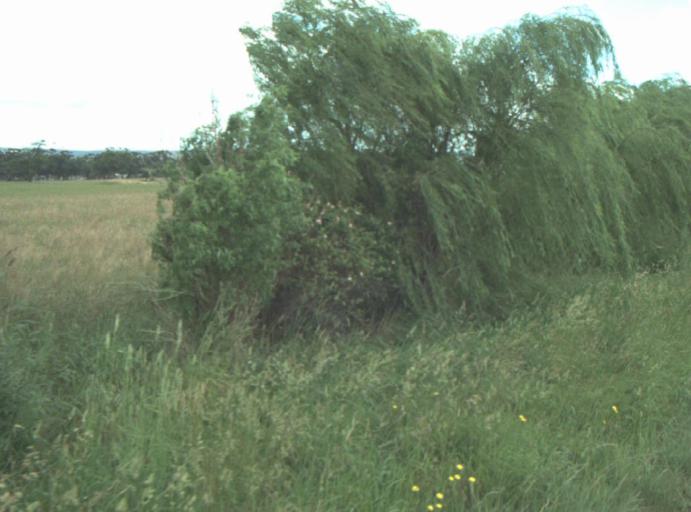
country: AU
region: Victoria
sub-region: Wyndham
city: Wyndham Vale
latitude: -37.8392
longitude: 144.3557
